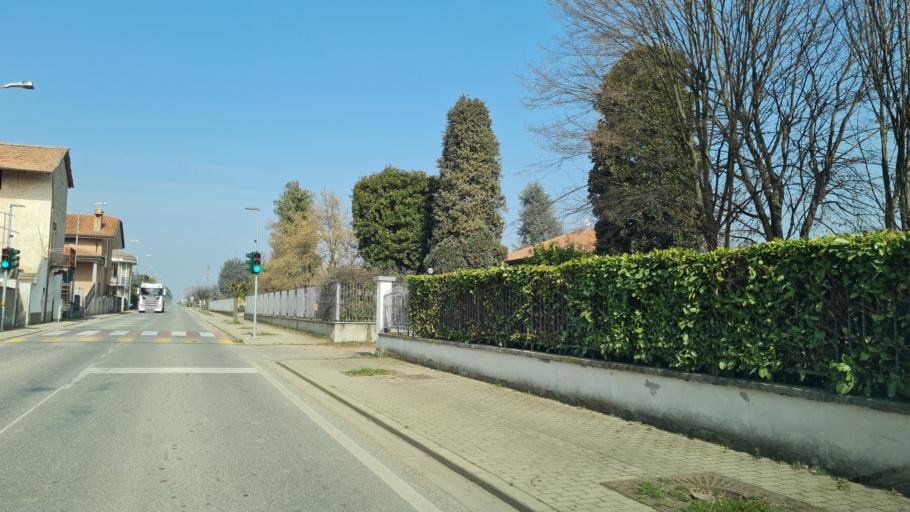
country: IT
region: Piedmont
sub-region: Provincia di Novara
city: Landiona
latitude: 45.5007
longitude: 8.4224
